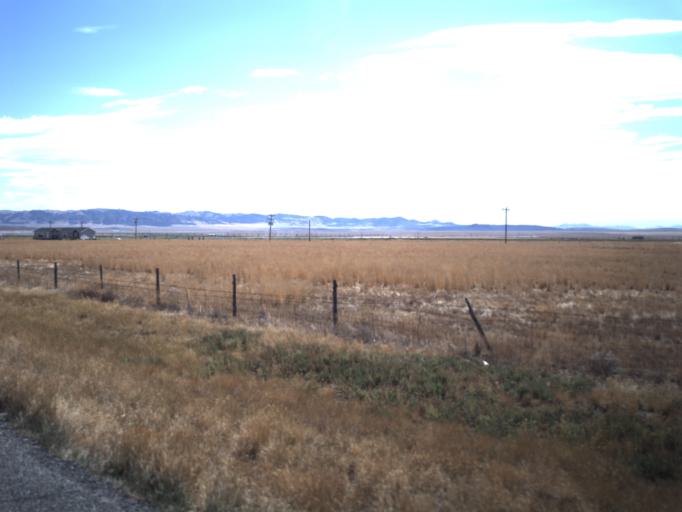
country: US
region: Idaho
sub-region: Oneida County
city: Malad City
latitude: 41.9665
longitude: -112.9151
